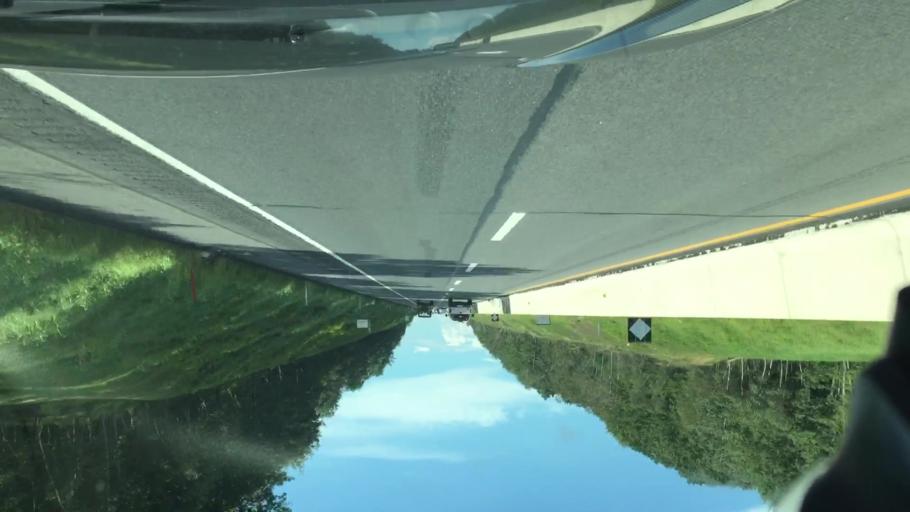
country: US
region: Pennsylvania
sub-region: Luzerne County
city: White Haven
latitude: 41.0659
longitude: -75.6913
